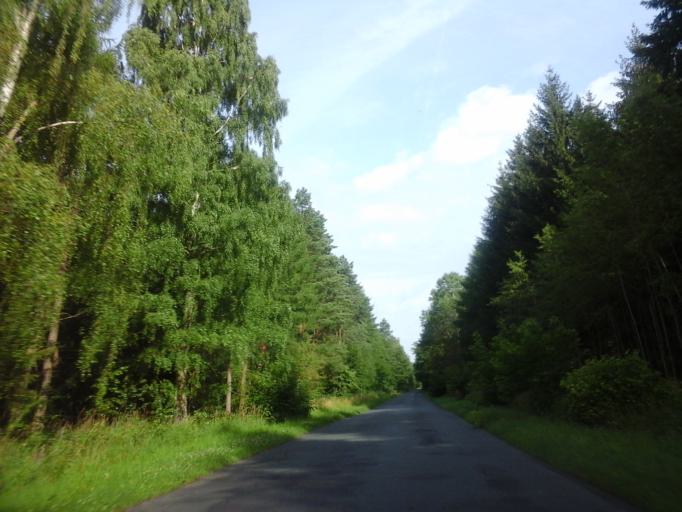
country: PL
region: West Pomeranian Voivodeship
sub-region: Powiat stargardzki
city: Dolice
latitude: 53.2321
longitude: 15.2598
